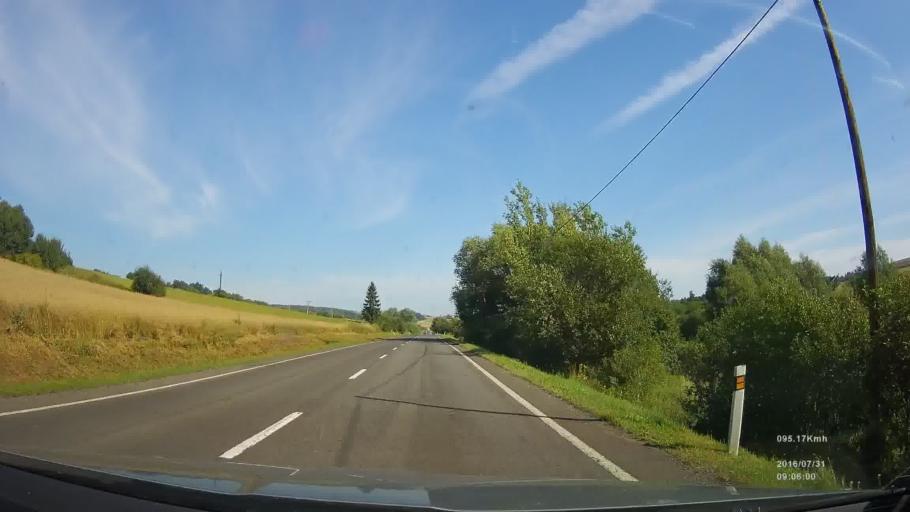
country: SK
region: Presovsky
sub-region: Okres Bardejov
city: Bardejov
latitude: 49.1643
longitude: 21.3121
